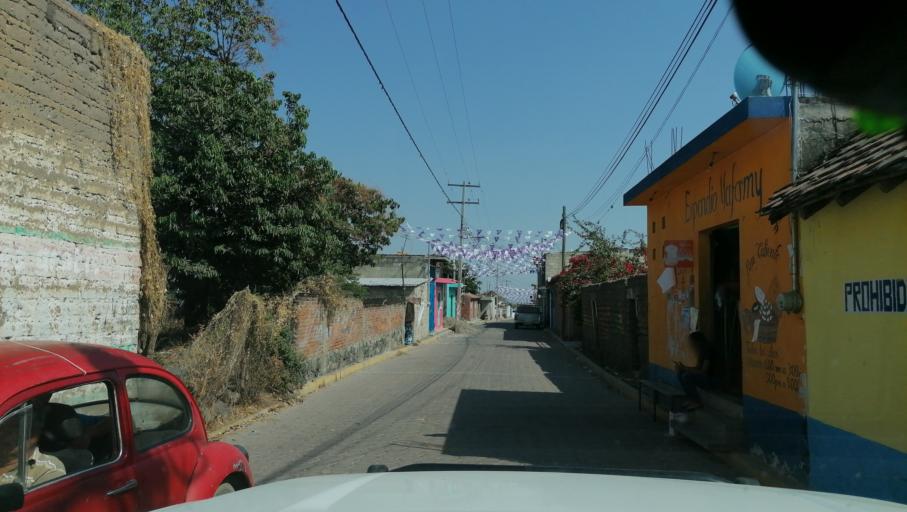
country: MX
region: Puebla
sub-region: Atzitzihuacan
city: San Miguel Aguacomulican
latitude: 18.8532
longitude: -98.5399
